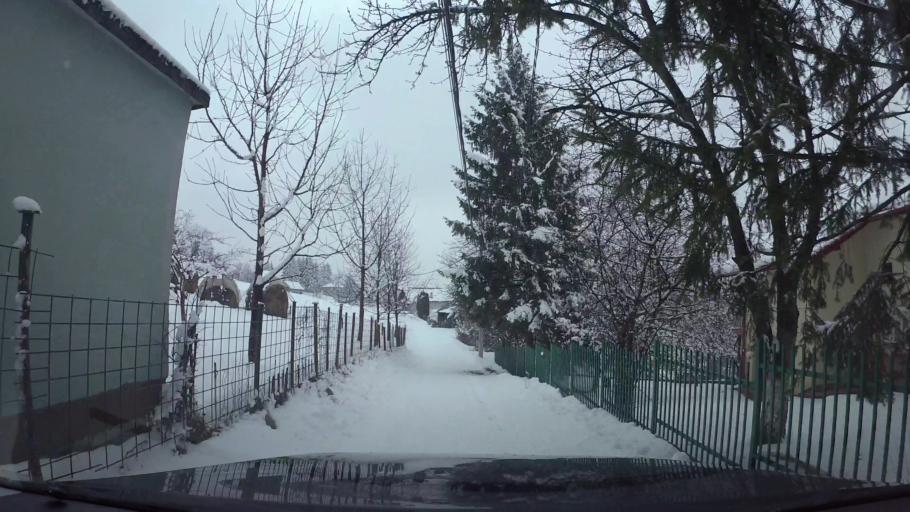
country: BA
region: Federation of Bosnia and Herzegovina
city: Hadzici
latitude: 43.8507
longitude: 18.2566
